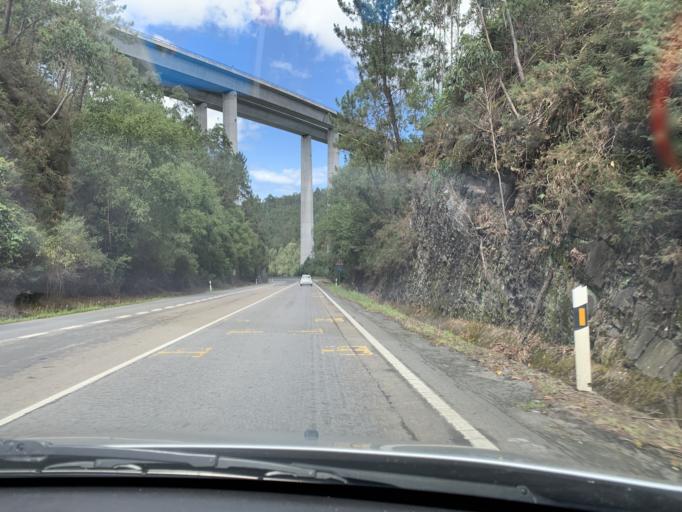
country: ES
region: Galicia
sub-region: Provincia de Lugo
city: Barreiros
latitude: 43.5037
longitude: -7.2712
